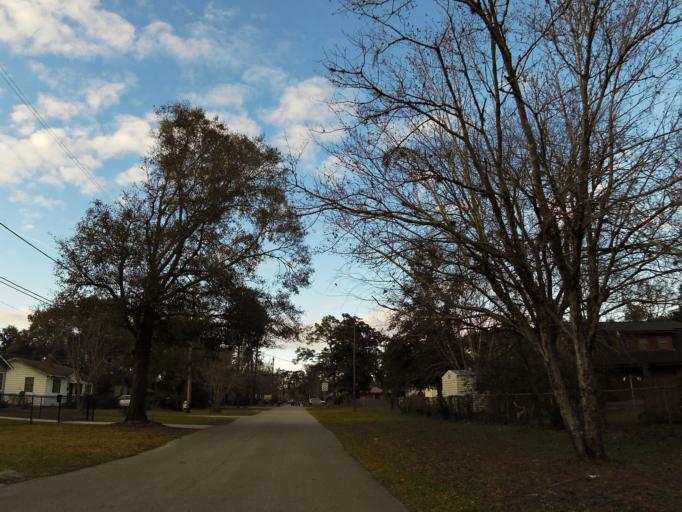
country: US
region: Florida
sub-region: Duval County
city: Jacksonville
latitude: 30.2948
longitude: -81.7284
